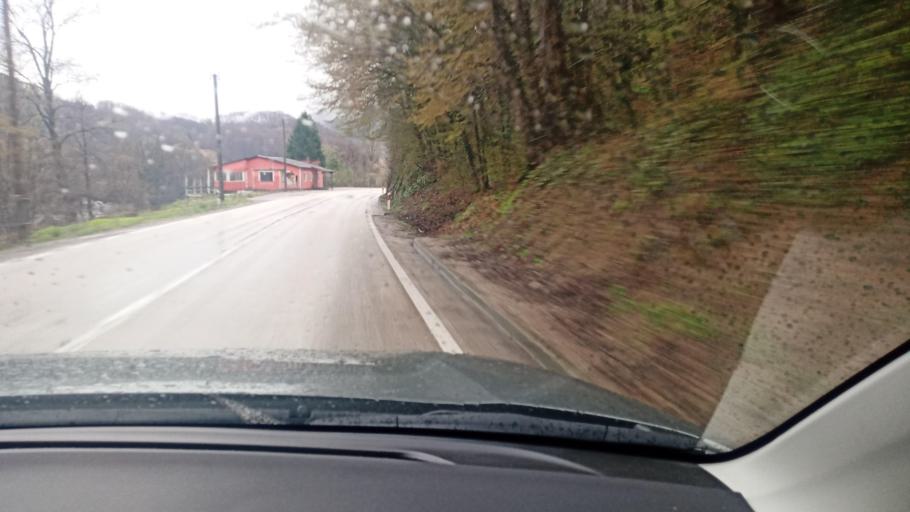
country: BA
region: Federation of Bosnia and Herzegovina
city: Otoka
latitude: 44.9278
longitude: 16.1567
